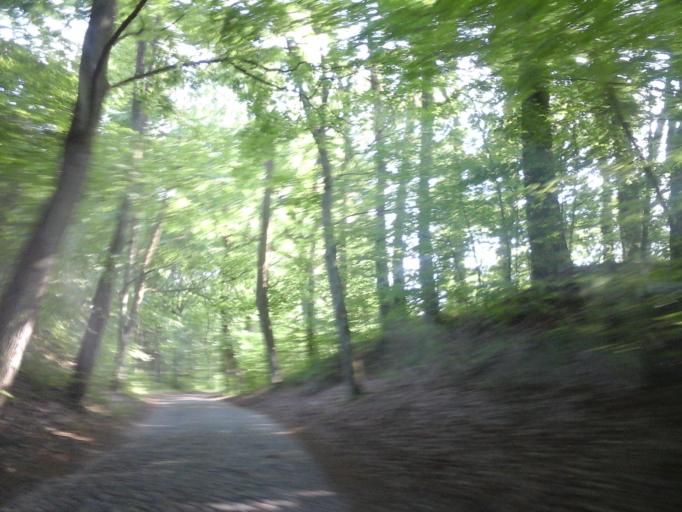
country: PL
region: West Pomeranian Voivodeship
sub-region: Powiat mysliborski
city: Barlinek
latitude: 53.0291
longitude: 15.2268
